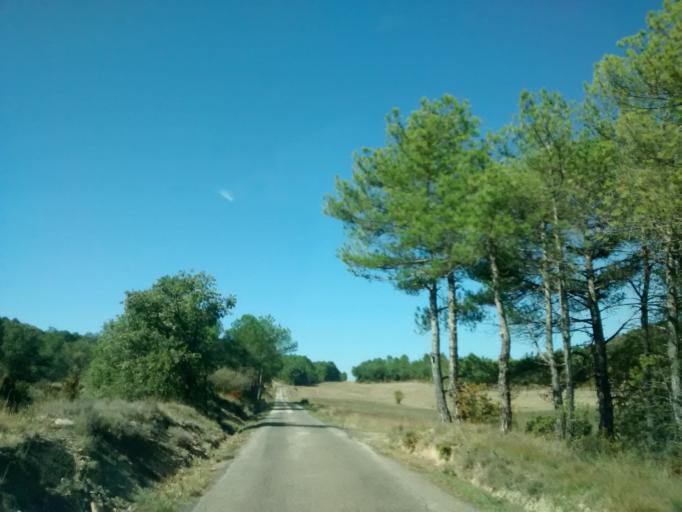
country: ES
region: Aragon
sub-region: Provincia de Huesca
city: Santa Cruz de la Seros
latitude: 42.4330
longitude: -0.6305
